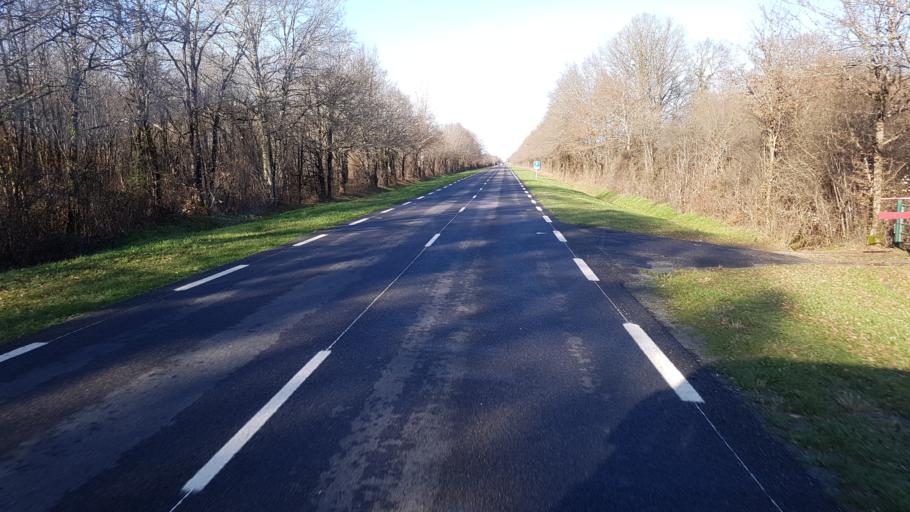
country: FR
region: Centre
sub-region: Departement du Loir-et-Cher
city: Salbris
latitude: 47.4596
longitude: 2.0421
